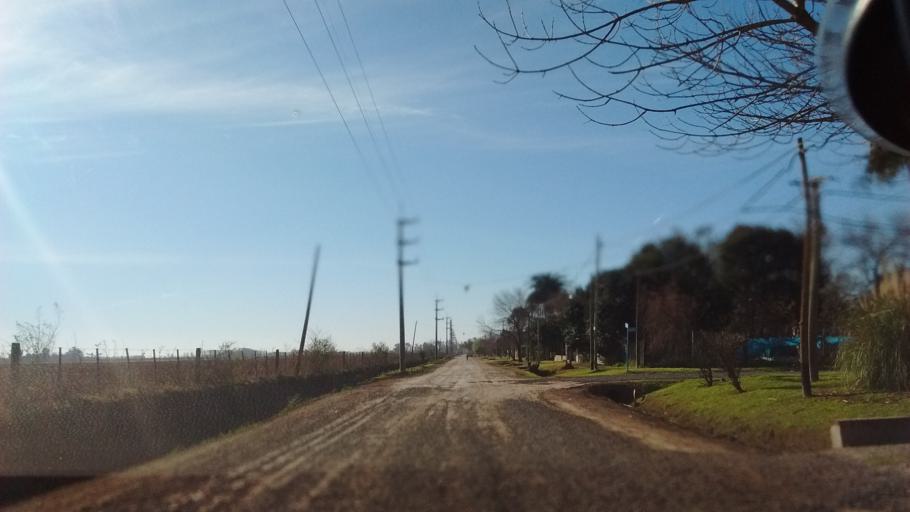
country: AR
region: Santa Fe
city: Funes
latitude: -32.9104
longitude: -60.8160
